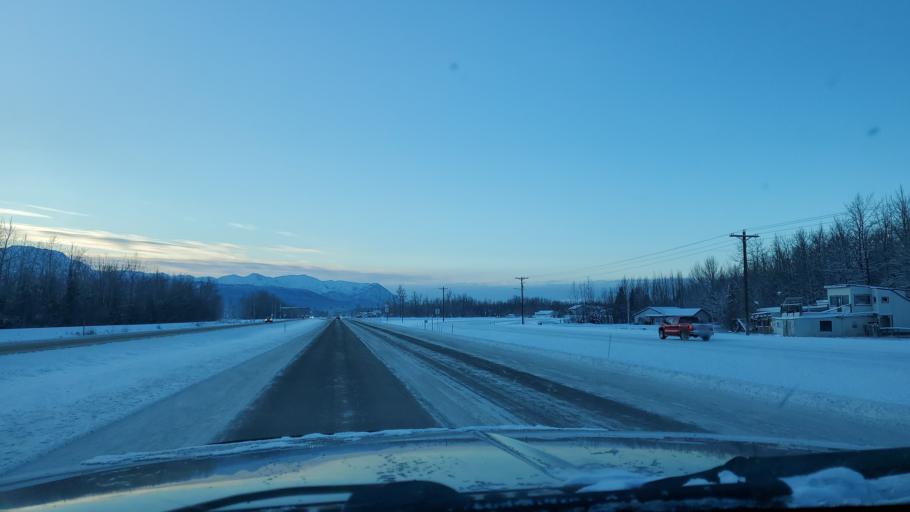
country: US
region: Alaska
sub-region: Matanuska-Susitna Borough
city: Palmer
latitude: 61.5741
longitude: -149.1457
